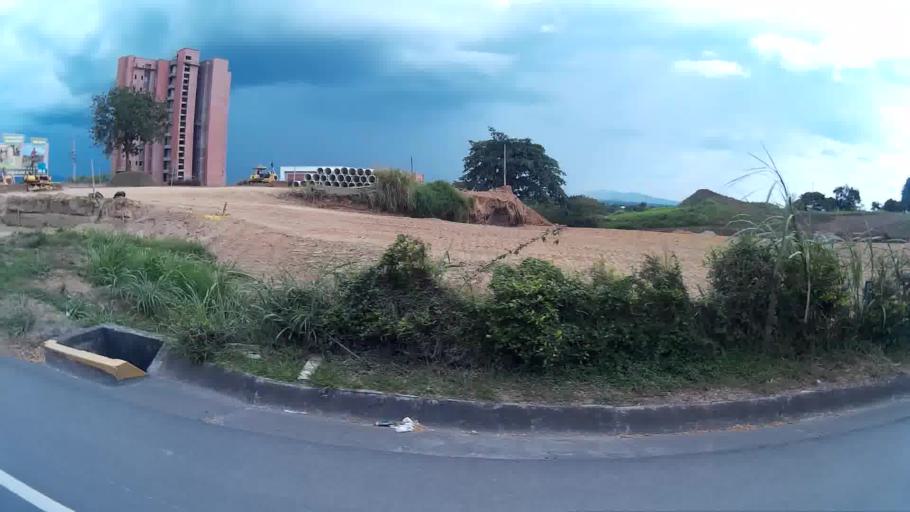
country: CO
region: Risaralda
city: Pereira
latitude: 4.8113
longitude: -75.7753
